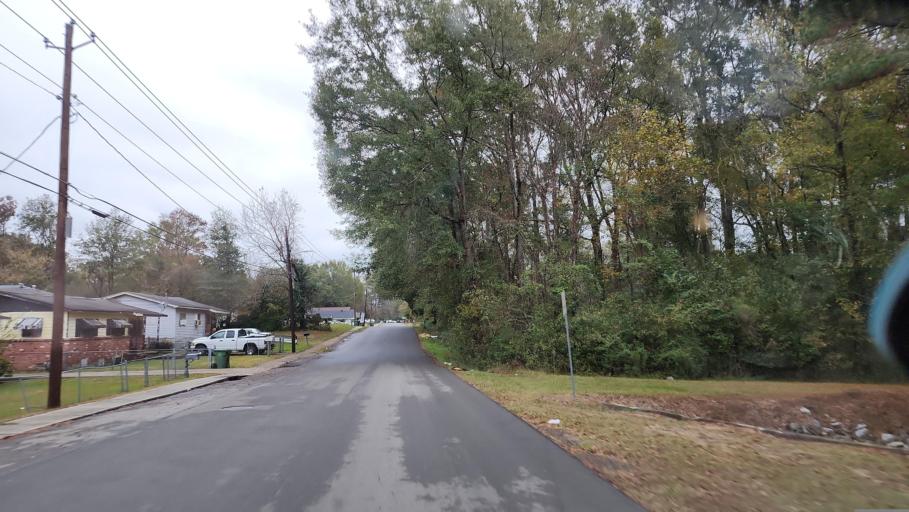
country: US
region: Mississippi
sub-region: Forrest County
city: Hattiesburg
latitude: 31.3049
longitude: -89.3024
